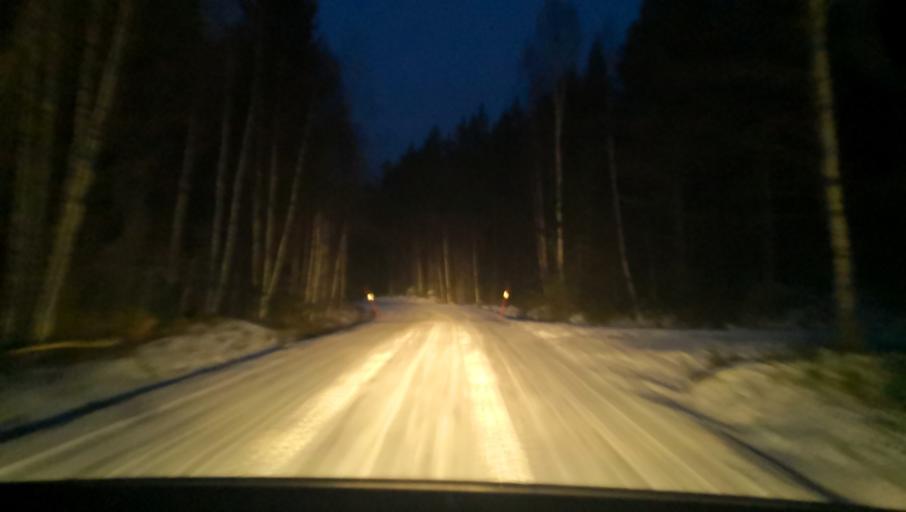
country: SE
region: Uppsala
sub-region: Heby Kommun
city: Tarnsjo
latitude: 60.2559
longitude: 16.7706
